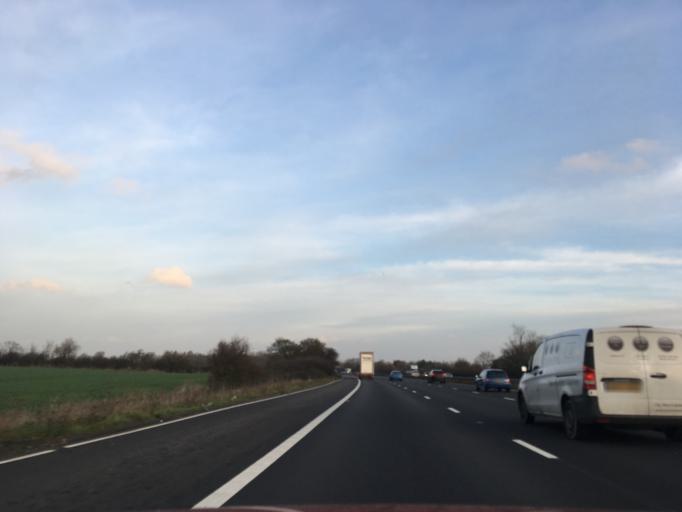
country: GB
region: England
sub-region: Gloucestershire
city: Uckington
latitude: 51.9456
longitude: -2.1261
